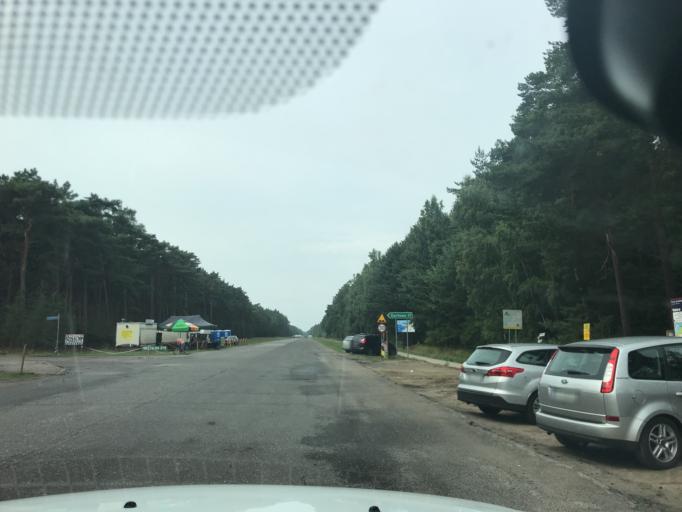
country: PL
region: West Pomeranian Voivodeship
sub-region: Powiat slawienski
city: Darlowo
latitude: 54.5265
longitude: 16.5099
